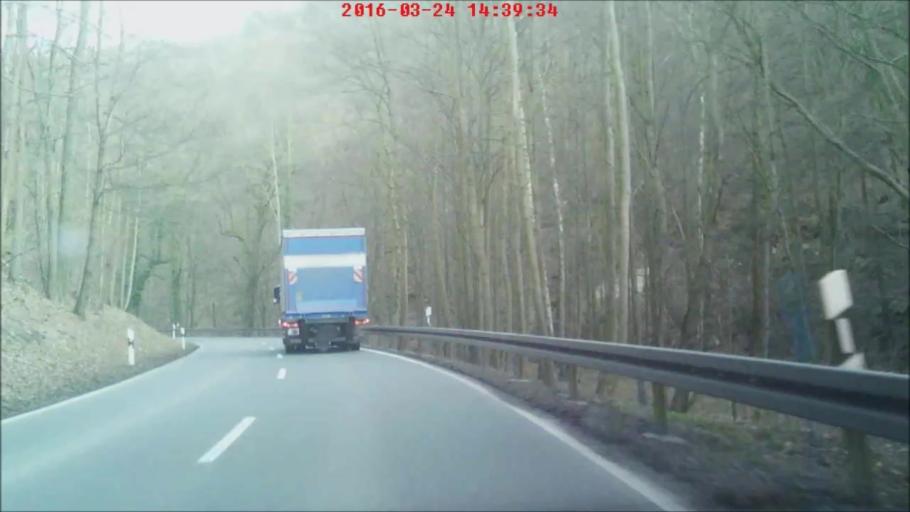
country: DE
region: Thuringia
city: Bad Blankenburg
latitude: 50.6691
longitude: 11.2516
